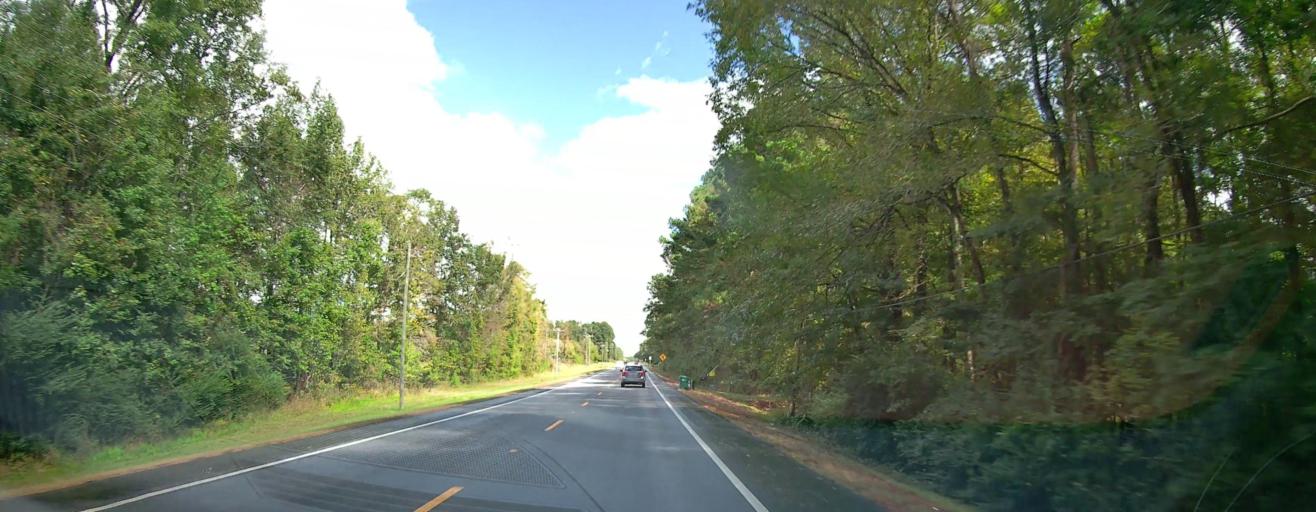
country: US
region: Georgia
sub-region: Baldwin County
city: Milledgeville
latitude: 33.0342
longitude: -83.3129
